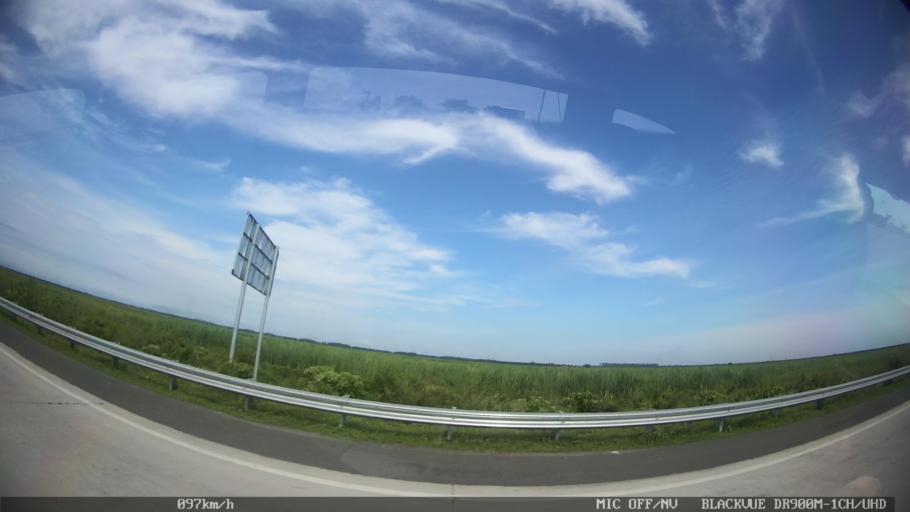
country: ID
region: North Sumatra
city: Binjai
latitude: 3.6732
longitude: 98.5349
